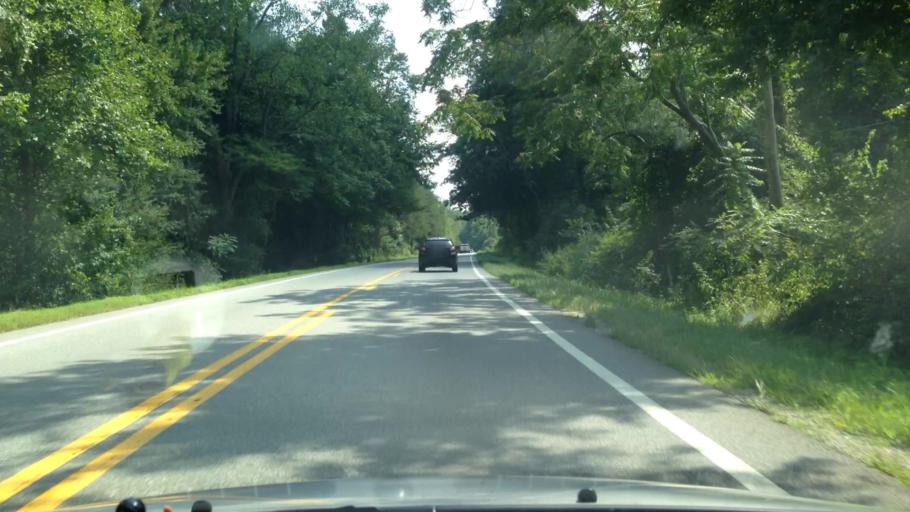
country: US
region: North Carolina
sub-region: Guilford County
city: Oak Ridge
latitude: 36.1836
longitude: -79.9868
